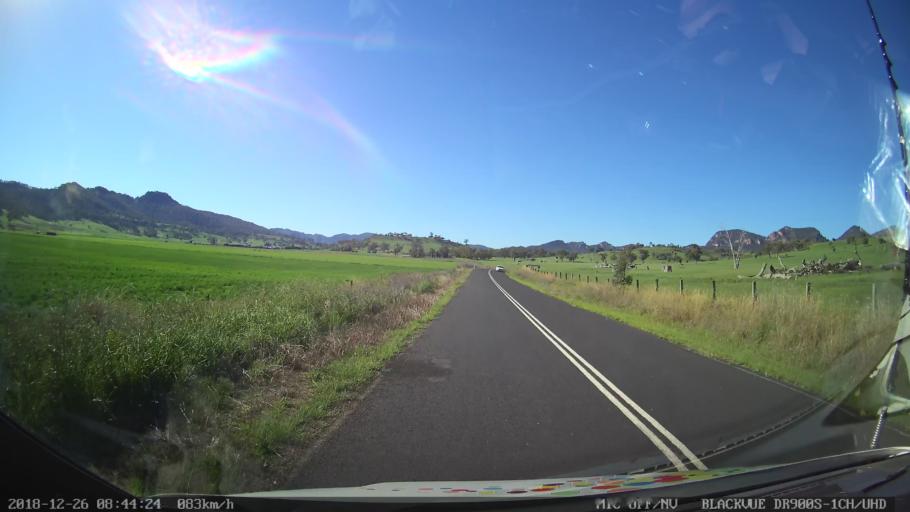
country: AU
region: New South Wales
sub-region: Mid-Western Regional
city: Kandos
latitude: -32.5142
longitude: 150.0809
